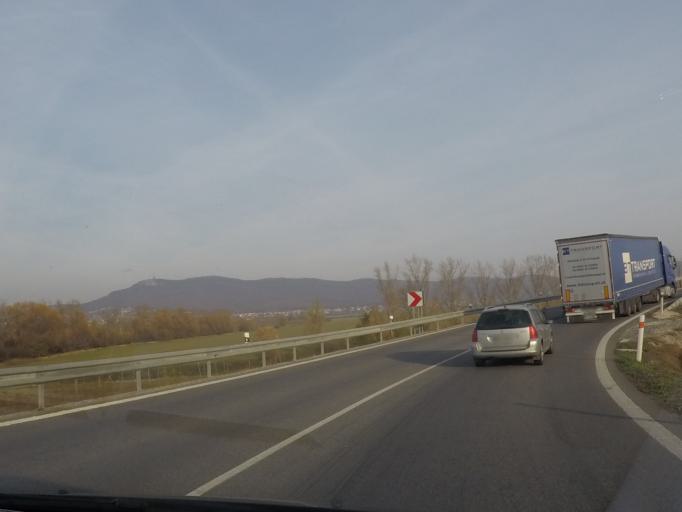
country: SK
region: Nitriansky
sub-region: Okres Nitra
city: Nitra
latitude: 48.3097
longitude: 18.1401
